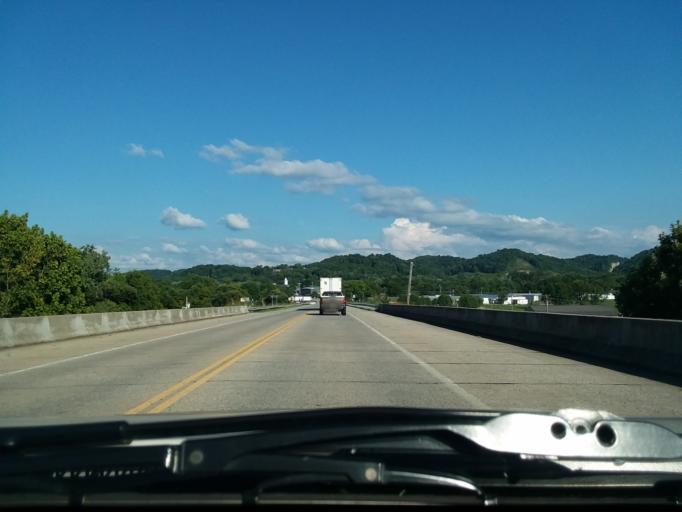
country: US
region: Tennessee
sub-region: Clay County
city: Celina
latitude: 36.5534
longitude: -85.5130
